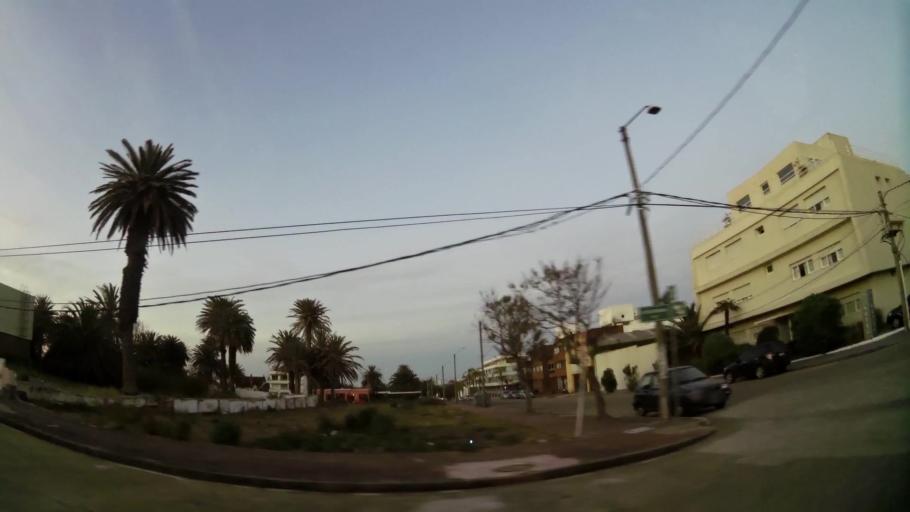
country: UY
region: Maldonado
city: Punta del Este
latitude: -34.9677
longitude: -54.9512
